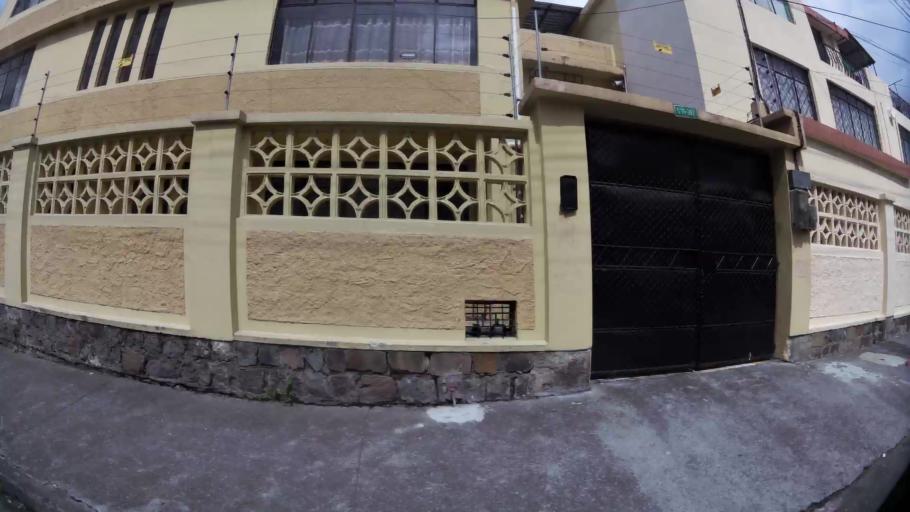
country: EC
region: Pichincha
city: Quito
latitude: -0.2465
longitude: -78.5332
